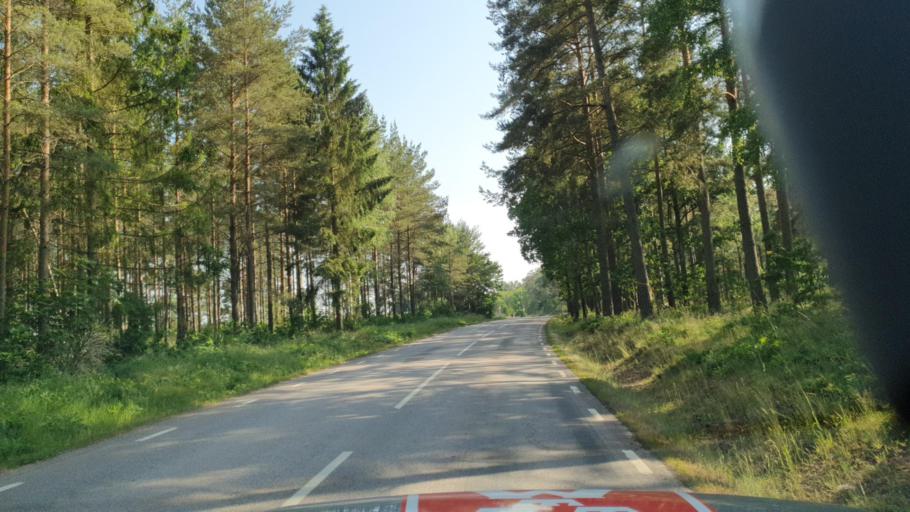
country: SE
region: Kalmar
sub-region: Kalmar Kommun
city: Ljungbyholm
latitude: 56.6595
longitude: 16.1598
